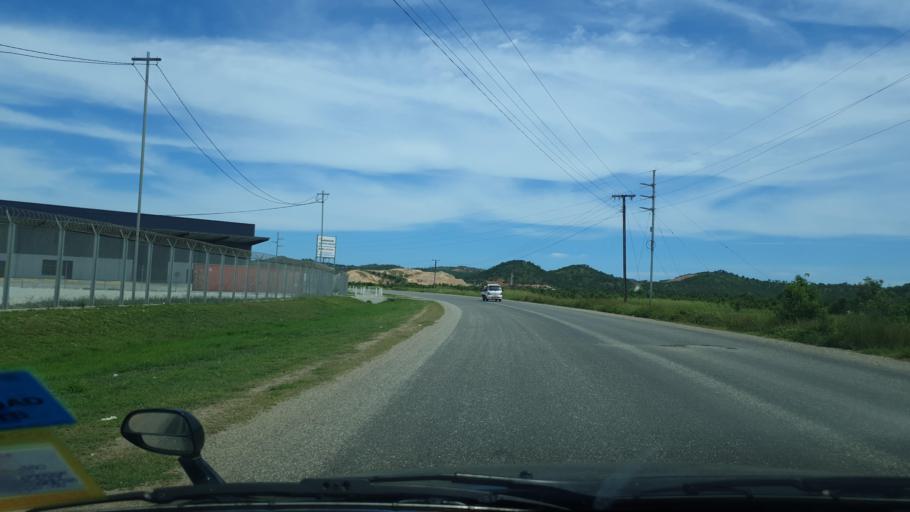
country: PG
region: National Capital
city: Port Moresby
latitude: -9.4138
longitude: 147.0725
